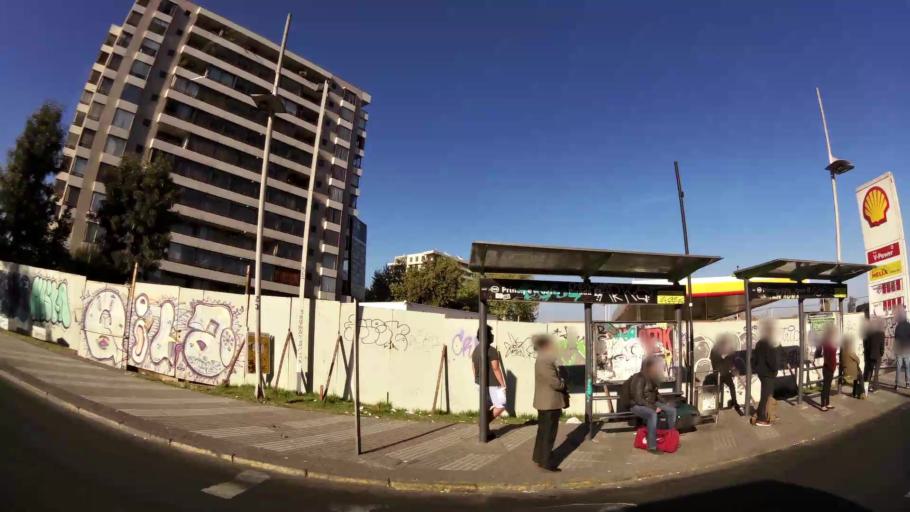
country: CL
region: Santiago Metropolitan
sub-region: Provincia de Santiago
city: Villa Presidente Frei, Nunoa, Santiago, Chile
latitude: -33.4393
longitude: -70.5723
